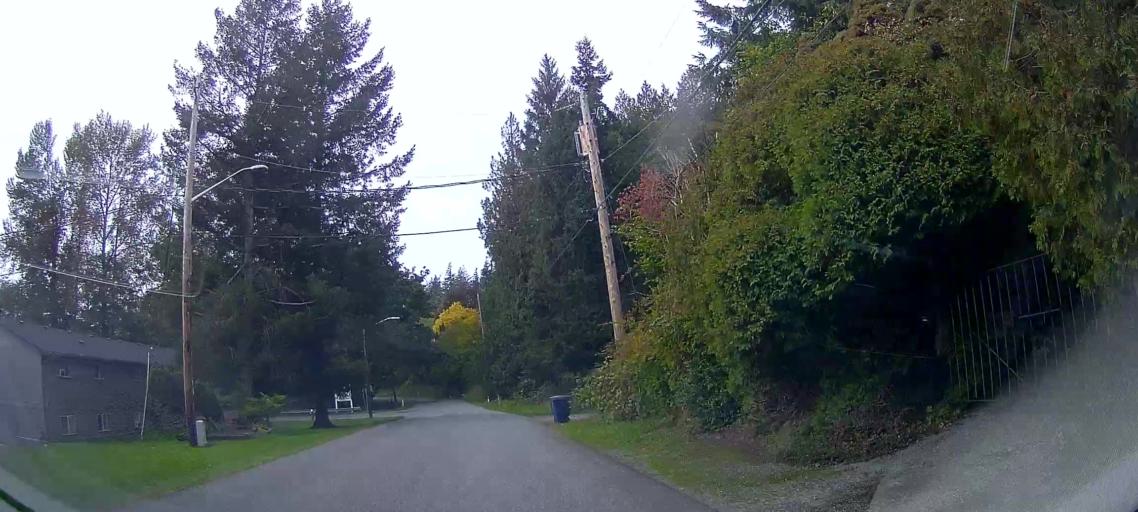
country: US
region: Washington
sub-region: Skagit County
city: Sedro-Woolley
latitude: 48.5209
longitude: -122.2296
